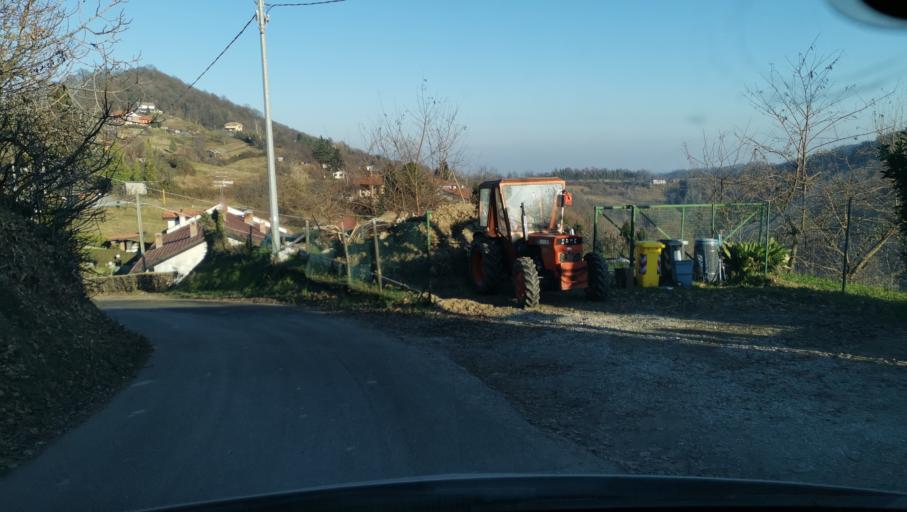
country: IT
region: Piedmont
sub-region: Provincia di Torino
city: Castagneto Po
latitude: 45.1427
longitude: 7.8740
